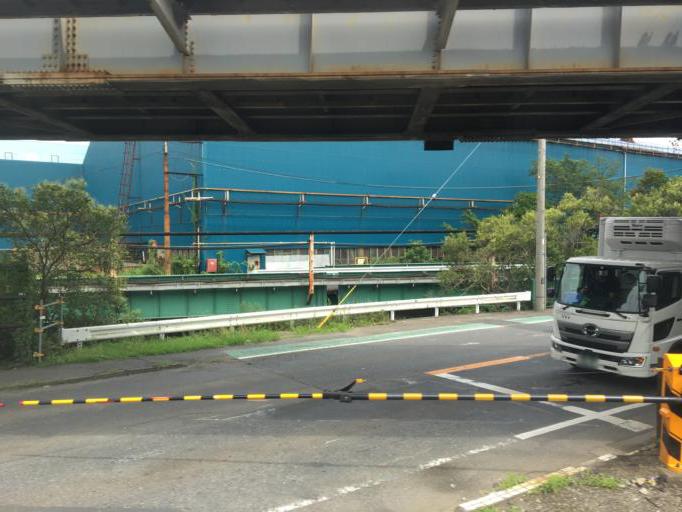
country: JP
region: Kanagawa
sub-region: Kawasaki-shi
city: Kawasaki
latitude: 35.5075
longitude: 139.7102
